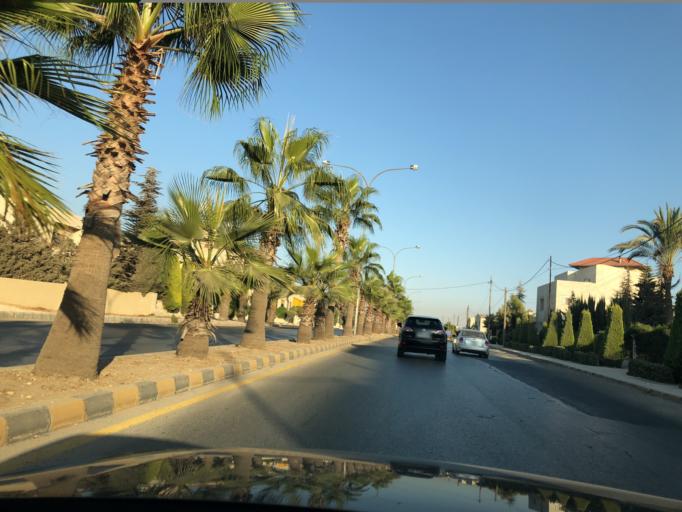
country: JO
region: Amman
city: Al Bunayyat ash Shamaliyah
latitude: 31.9433
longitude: 35.8773
